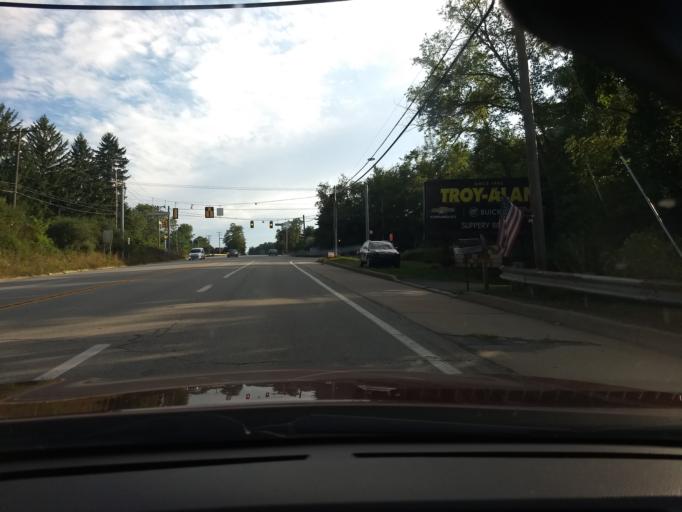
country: US
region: Pennsylvania
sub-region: Armstrong County
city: Freeport
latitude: 40.6656
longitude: -79.7032
